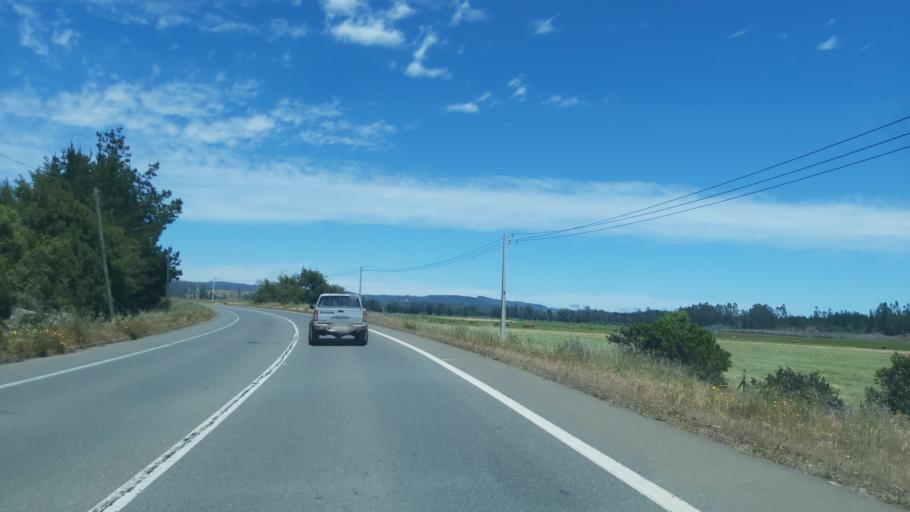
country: CL
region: Maule
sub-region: Provincia de Talca
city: Constitucion
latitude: -35.2890
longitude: -72.3669
